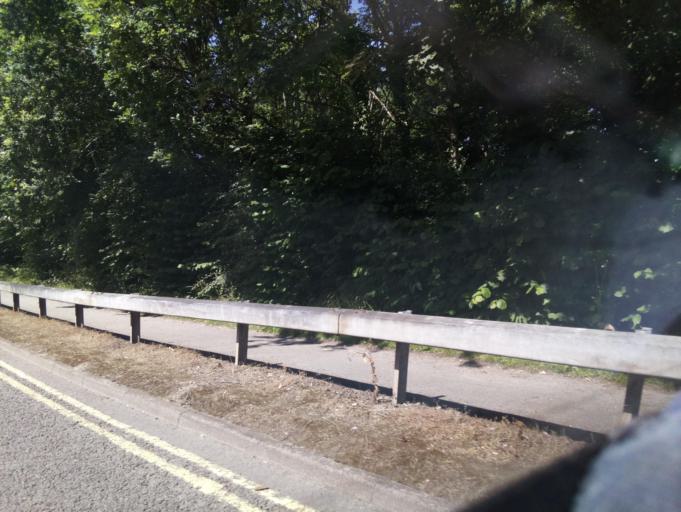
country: GB
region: England
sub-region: Derby
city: Derby
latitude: 52.9338
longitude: -1.4966
